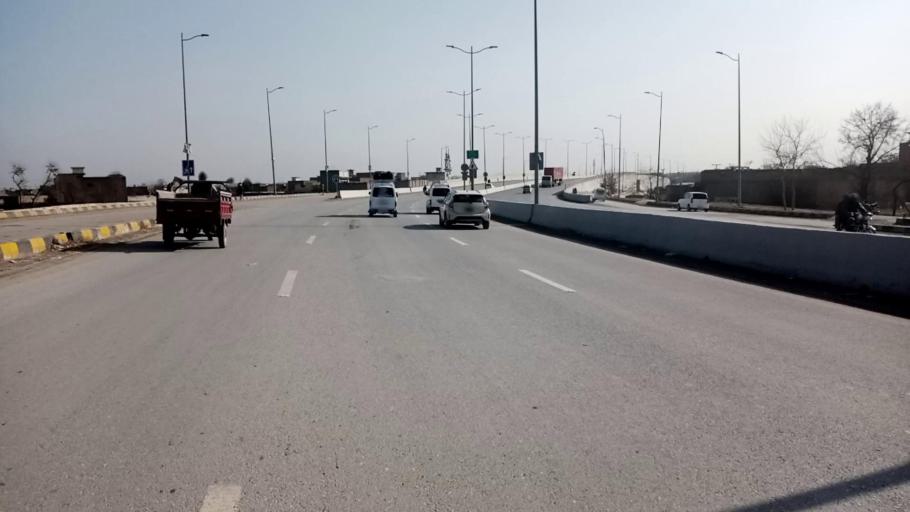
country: PK
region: Khyber Pakhtunkhwa
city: Peshawar
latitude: 34.0386
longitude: 71.5397
